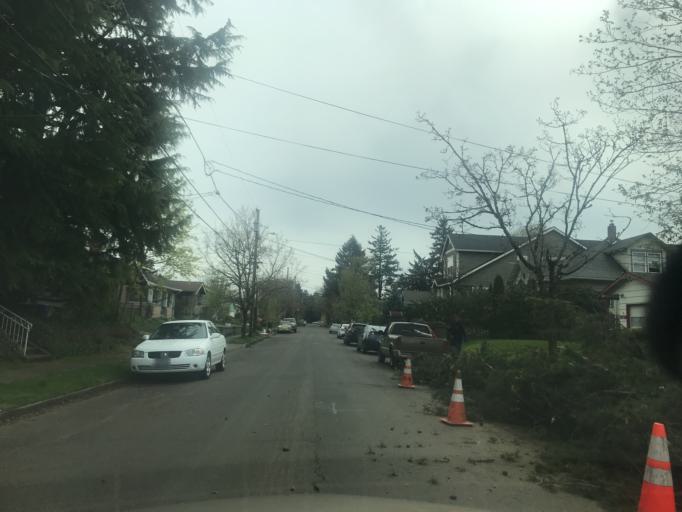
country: US
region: Oregon
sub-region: Multnomah County
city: Lents
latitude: 45.4931
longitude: -122.5940
